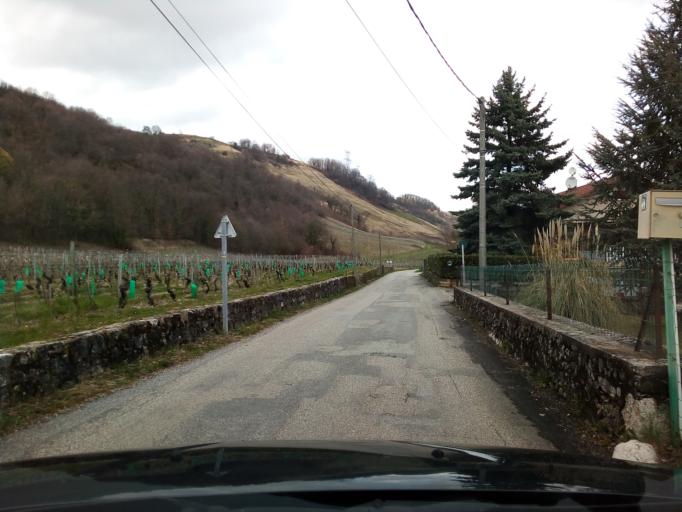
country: FR
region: Rhone-Alpes
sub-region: Departement de l'Isere
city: Chapareillan
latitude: 45.4759
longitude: 5.9820
